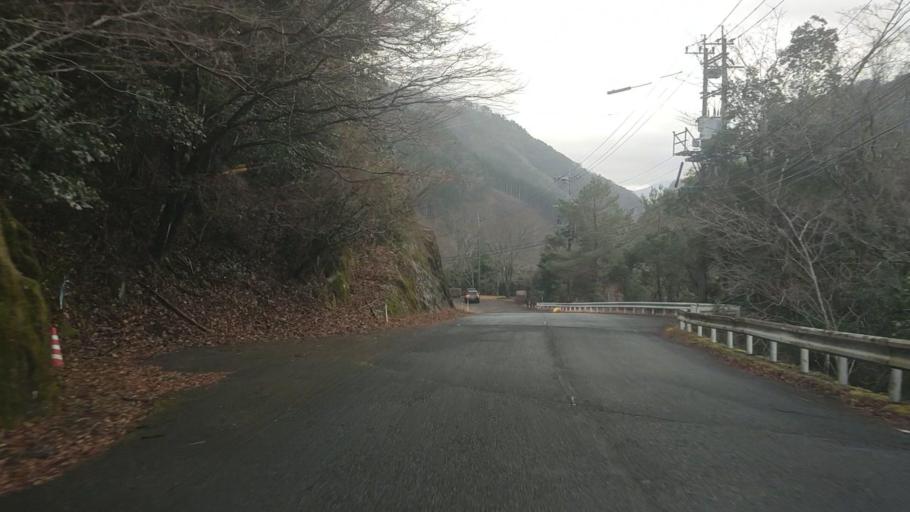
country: JP
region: Kumamoto
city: Matsubase
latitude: 32.4900
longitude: 130.9011
